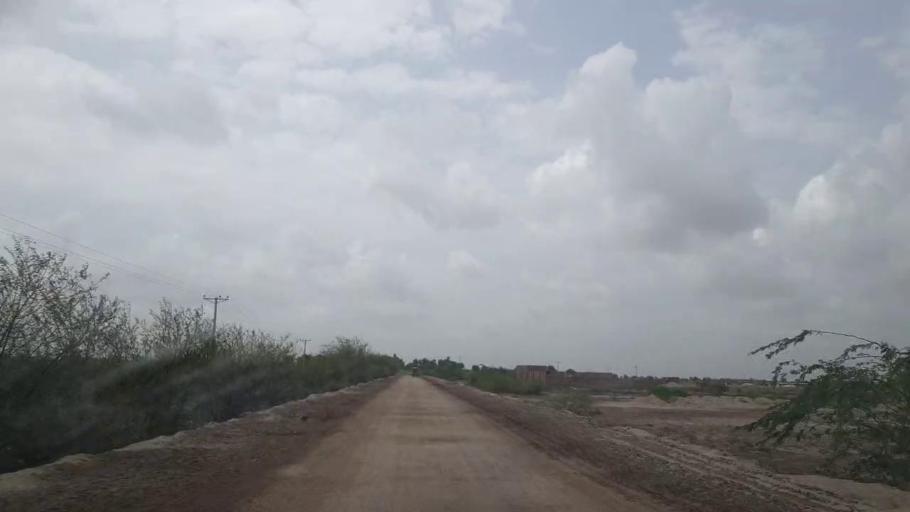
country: PK
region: Sindh
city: Naukot
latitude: 24.9450
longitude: 69.2586
